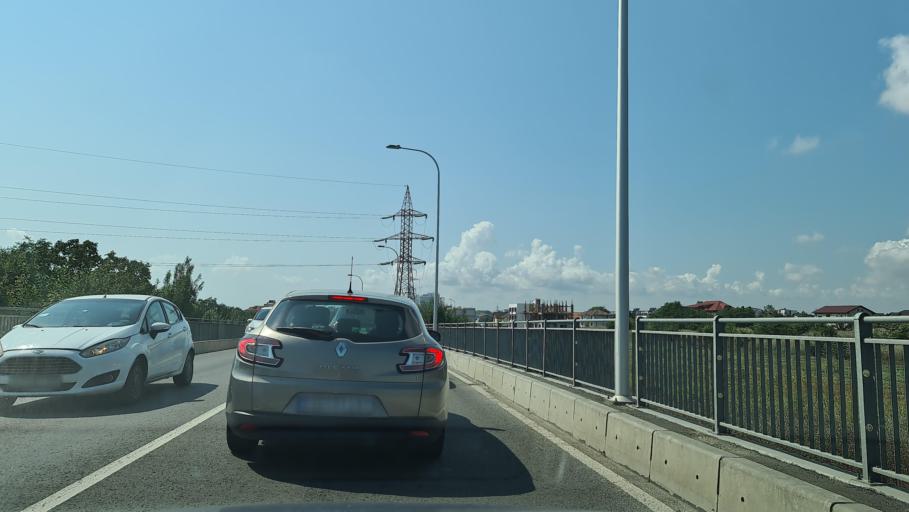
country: RO
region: Constanta
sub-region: Oras Eforie
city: Eforie Nord
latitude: 44.0863
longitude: 28.6399
